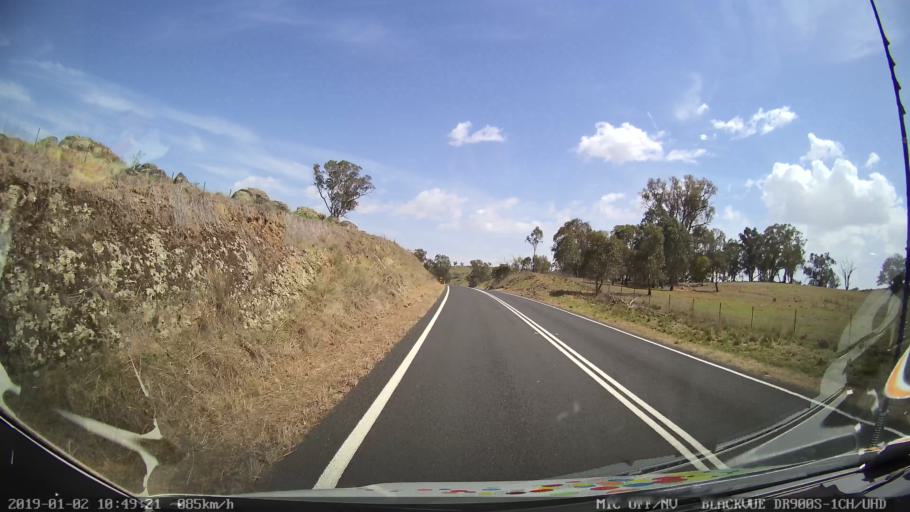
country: AU
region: New South Wales
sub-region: Cootamundra
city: Cootamundra
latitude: -34.7256
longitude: 148.2769
